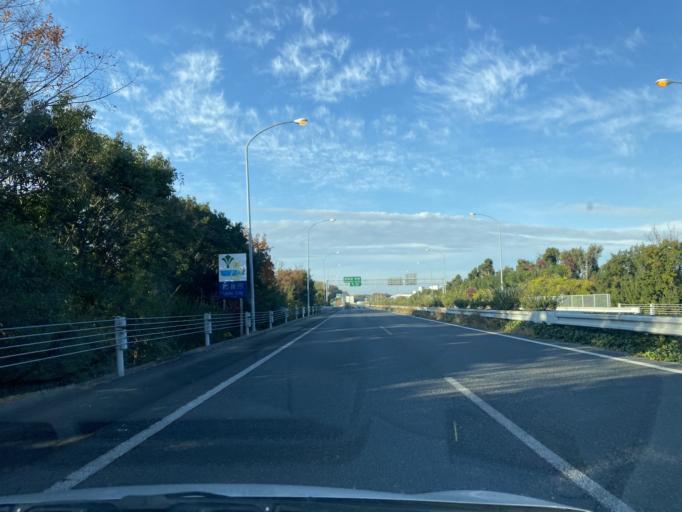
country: JP
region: Osaka
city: Izumi
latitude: 34.4335
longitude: 135.4458
